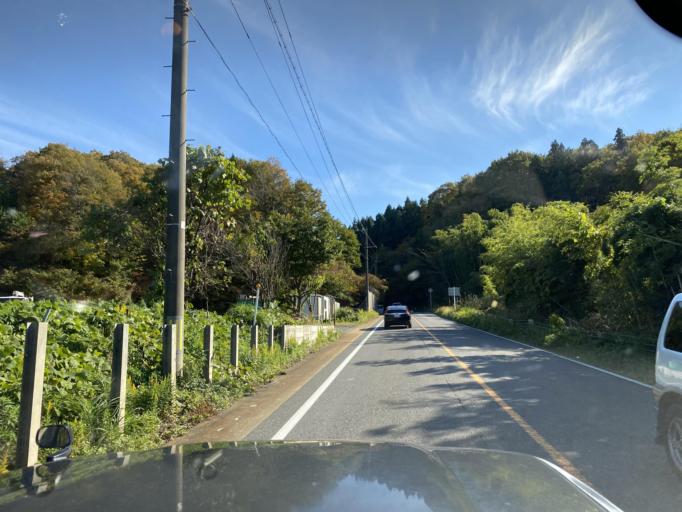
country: JP
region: Niigata
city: Niitsu-honcho
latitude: 37.7500
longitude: 139.1074
